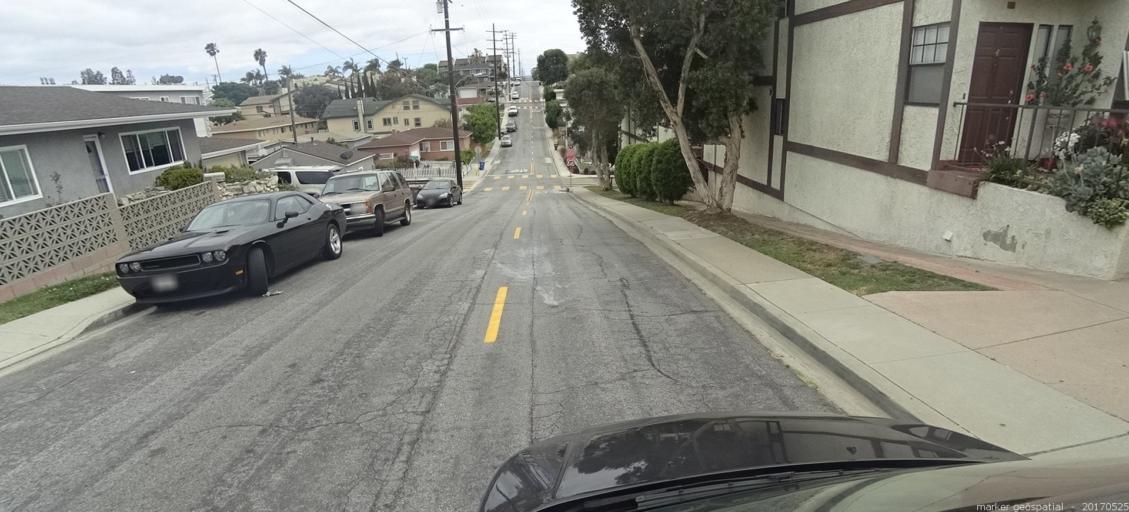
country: US
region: California
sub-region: Los Angeles County
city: Redondo Beach
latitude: 33.8714
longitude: -118.3749
